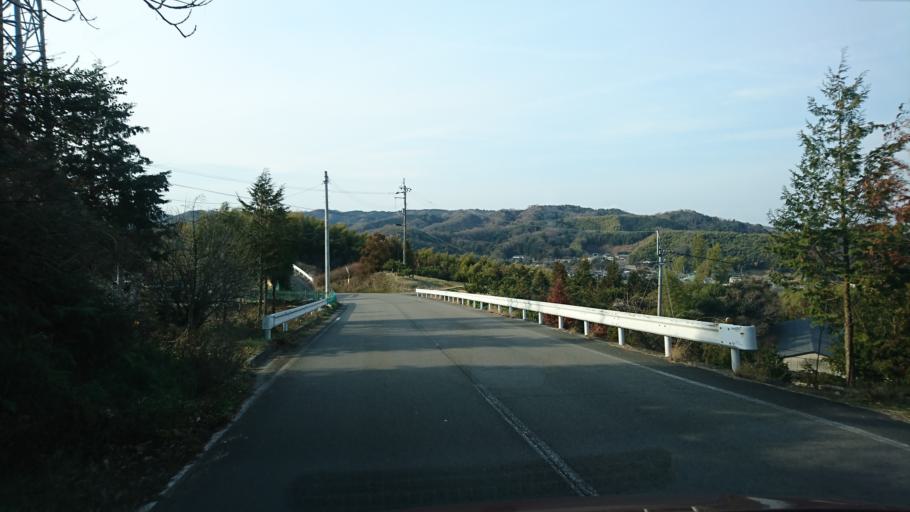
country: JP
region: Ehime
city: Hojo
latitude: 34.0234
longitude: 132.9659
